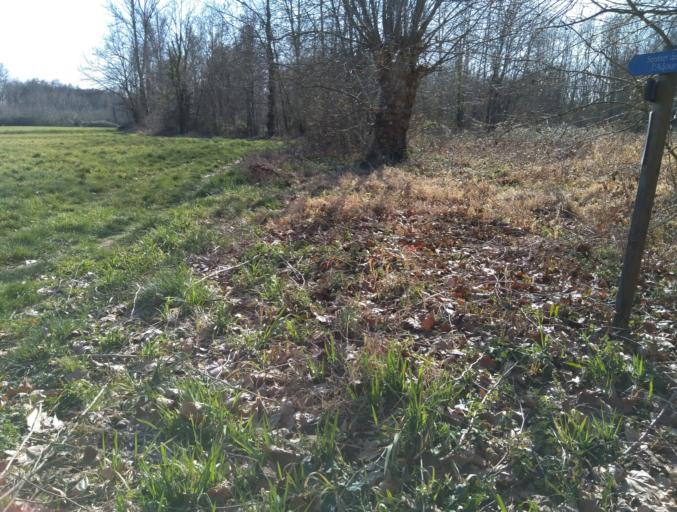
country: FR
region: Midi-Pyrenees
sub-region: Departement des Hautes-Pyrenees
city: Maubourguet
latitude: 43.4849
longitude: 0.0354
